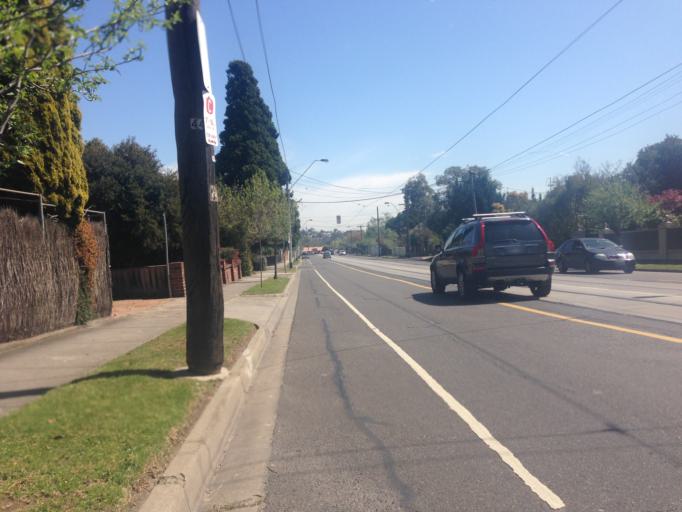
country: AU
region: Victoria
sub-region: Boroondara
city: Kew East
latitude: -37.7929
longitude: 145.0686
